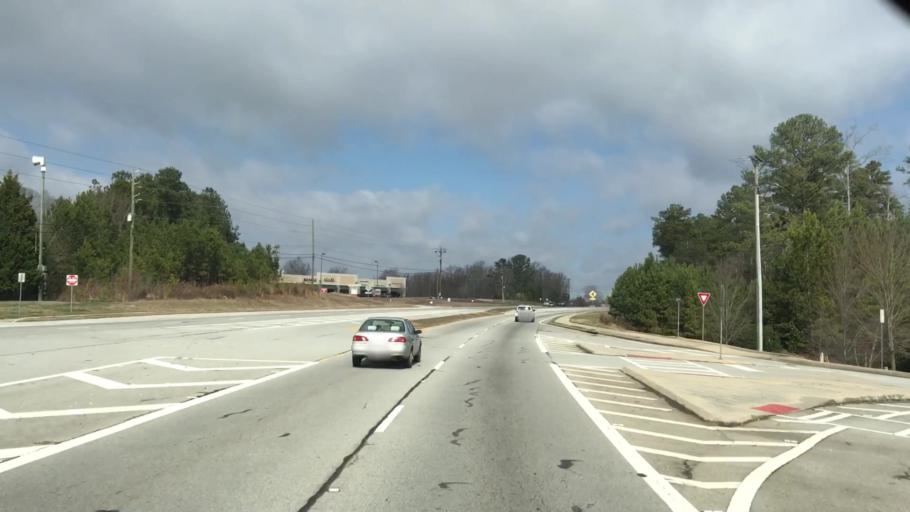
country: US
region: Georgia
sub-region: Hall County
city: Oakwood
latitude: 34.1982
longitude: -83.8588
